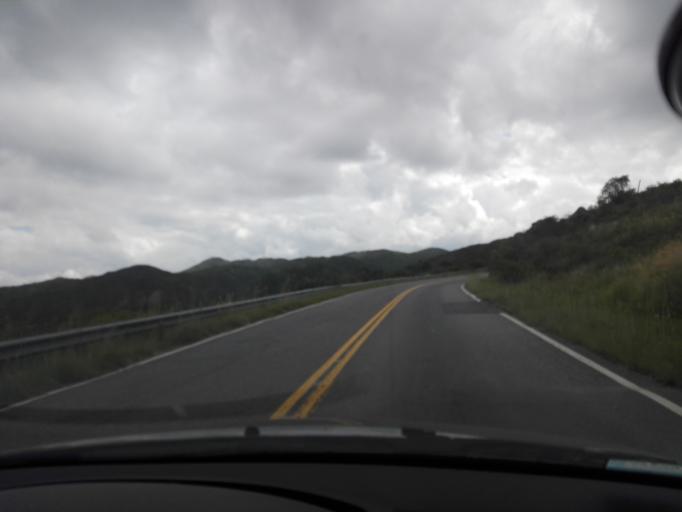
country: AR
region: Cordoba
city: Alta Gracia
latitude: -31.5932
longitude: -64.5212
